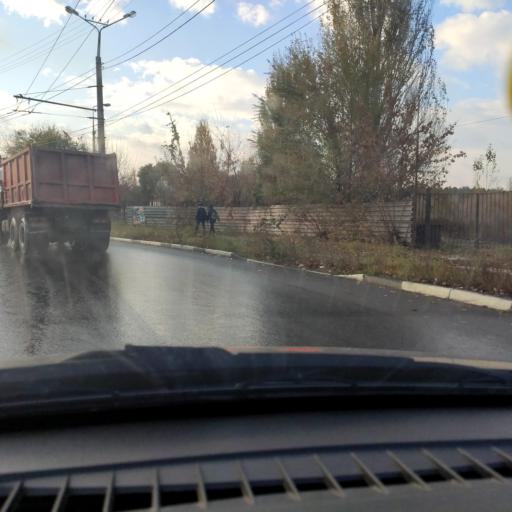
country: RU
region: Samara
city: Tol'yatti
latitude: 53.5292
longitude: 49.3959
